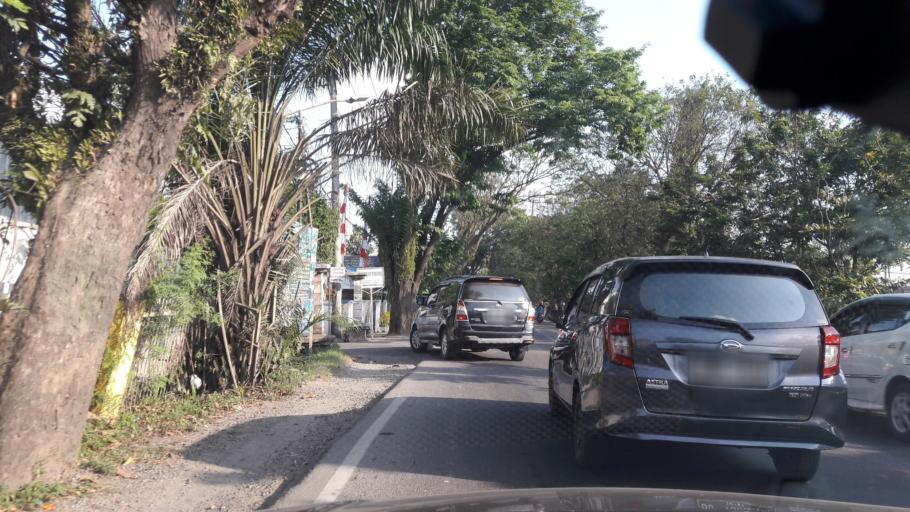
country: ID
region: South Sumatra
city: Plaju
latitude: -3.0115
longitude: 104.7231
